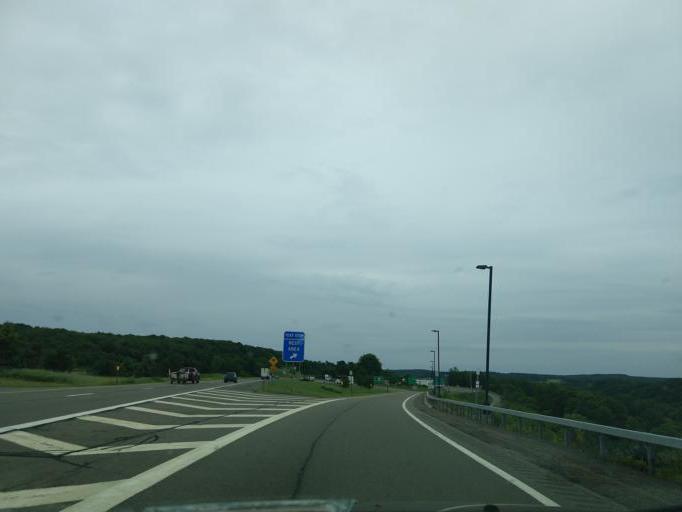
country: US
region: New York
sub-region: Chenango County
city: Lakeview
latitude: 42.3780
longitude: -75.9949
